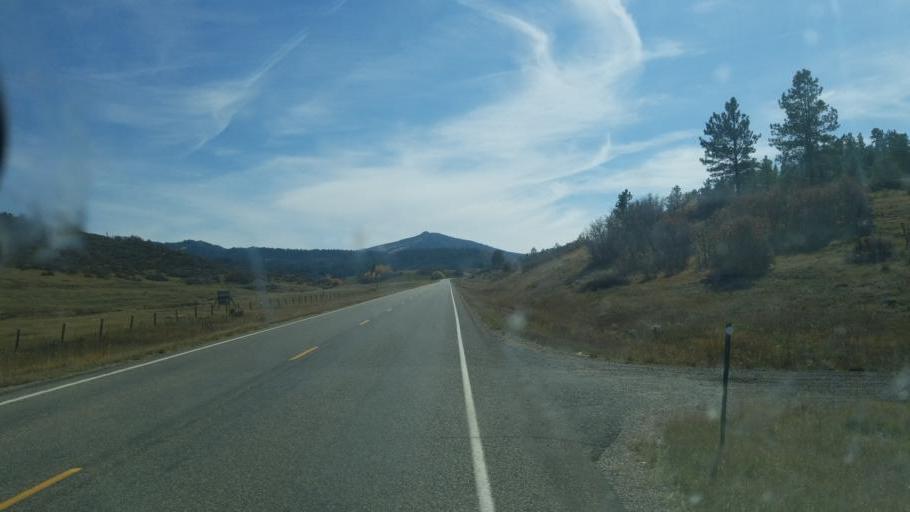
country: US
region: New Mexico
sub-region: Rio Arriba County
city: Dulce
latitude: 37.0079
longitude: -106.7982
